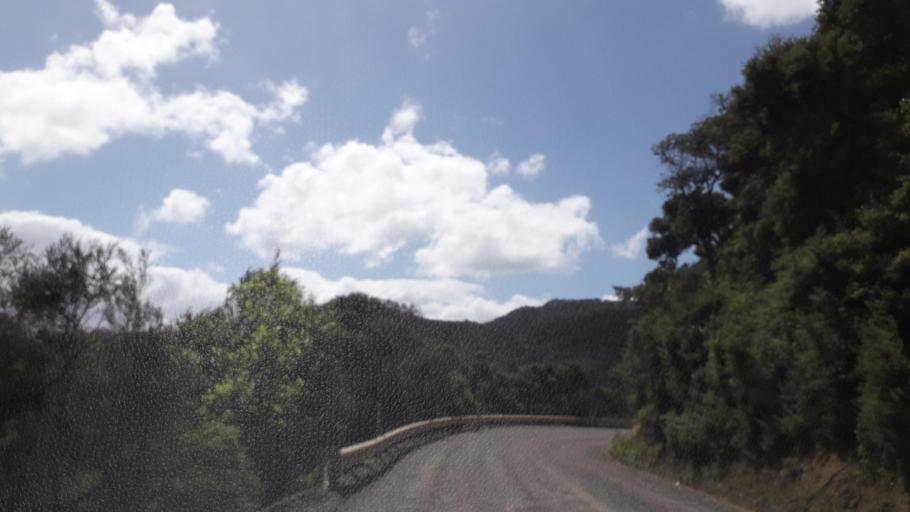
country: NZ
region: Northland
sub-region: Far North District
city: Paihia
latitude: -35.2604
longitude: 174.2643
